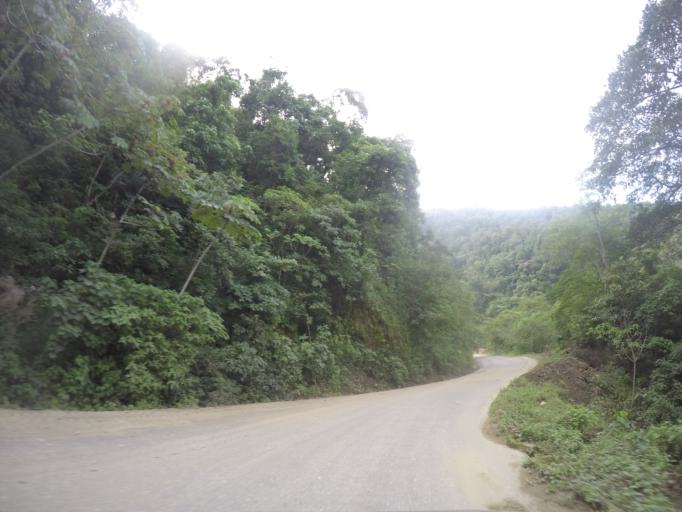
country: MX
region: Oaxaca
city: Pluma Hidalgo
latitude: 15.9481
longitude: -96.4397
